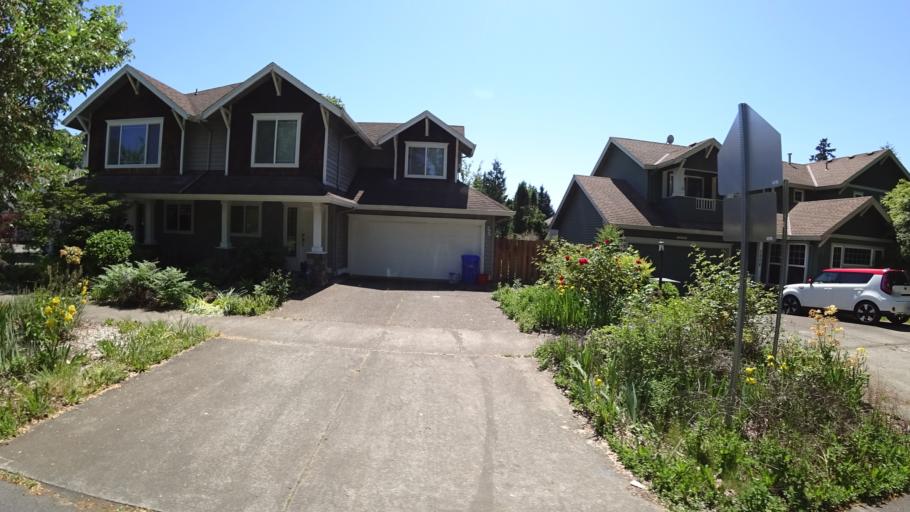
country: US
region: Oregon
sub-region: Washington County
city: Rockcreek
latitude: 45.5268
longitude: -122.9081
